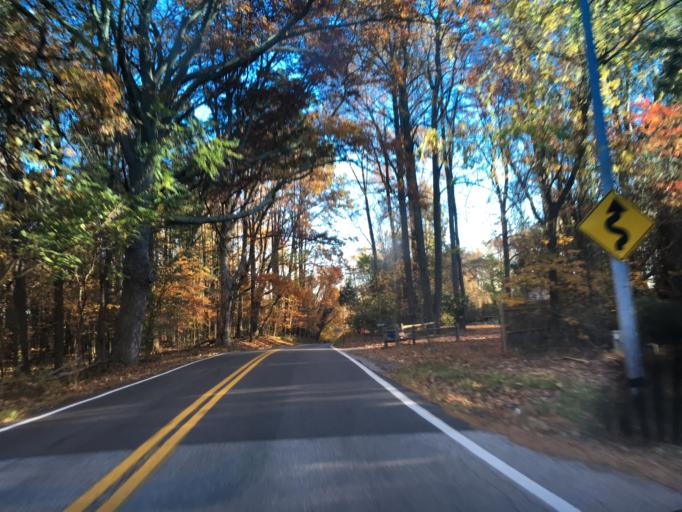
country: US
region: Maryland
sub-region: Baltimore County
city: Owings Mills
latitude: 39.4604
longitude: -76.7701
